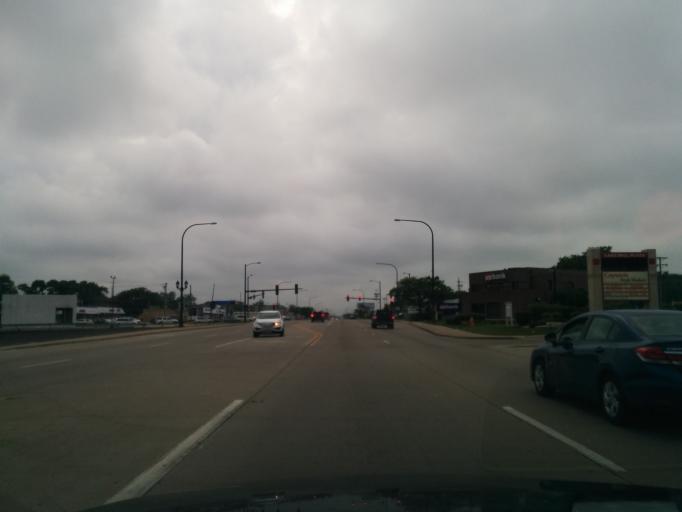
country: US
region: Illinois
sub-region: DuPage County
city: Addison
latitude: 41.9378
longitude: -88.0016
